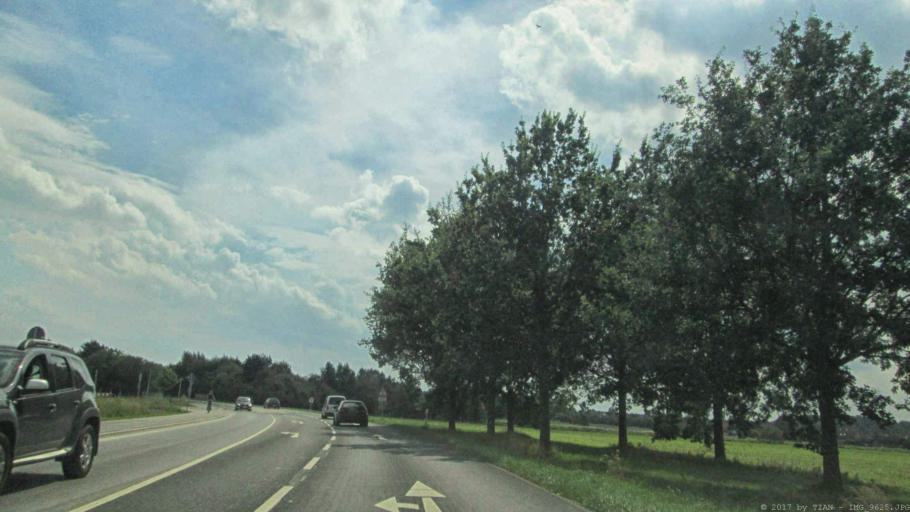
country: DE
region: Lower Saxony
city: Wolfsburg
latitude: 52.4252
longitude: 10.8292
